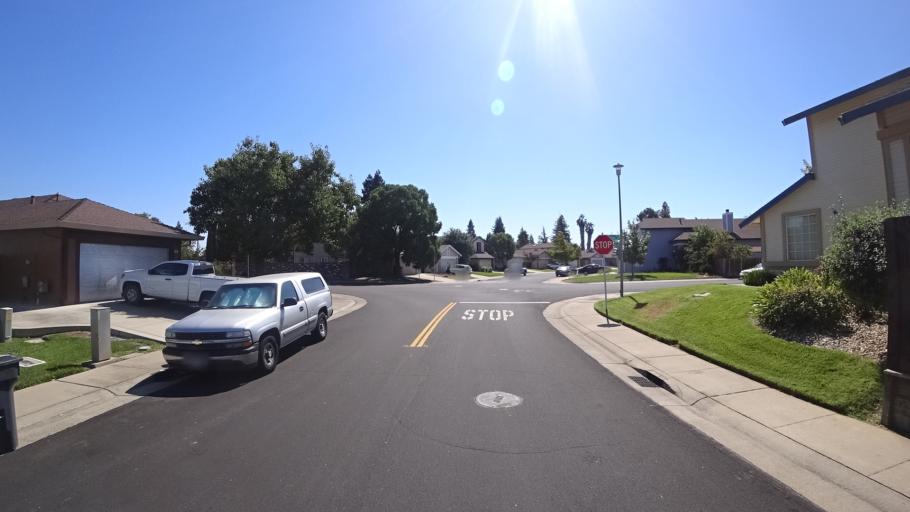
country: US
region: California
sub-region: Sacramento County
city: Laguna
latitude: 38.4345
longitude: -121.4392
